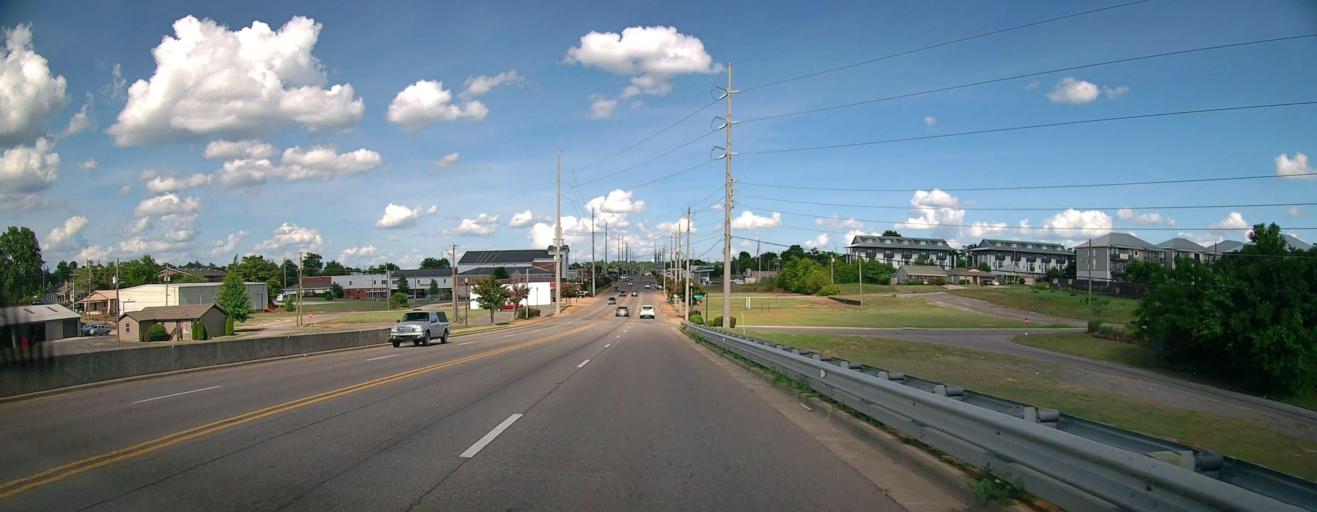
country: US
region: Alabama
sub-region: Tuscaloosa County
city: Holt
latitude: 33.2061
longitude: -87.5119
